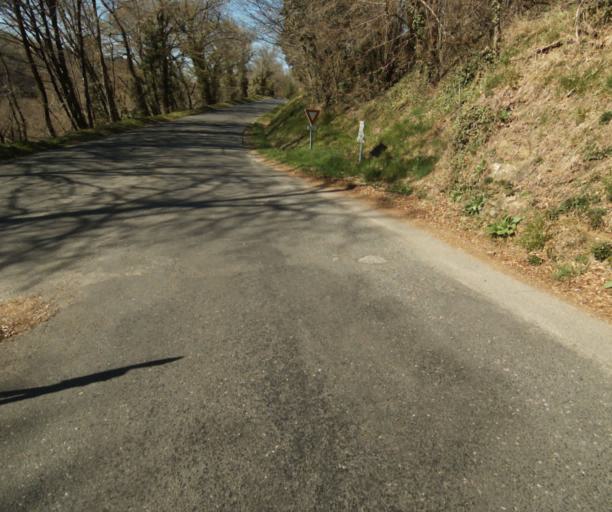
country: FR
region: Limousin
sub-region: Departement de la Correze
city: Tulle
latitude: 45.2828
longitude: 1.7322
